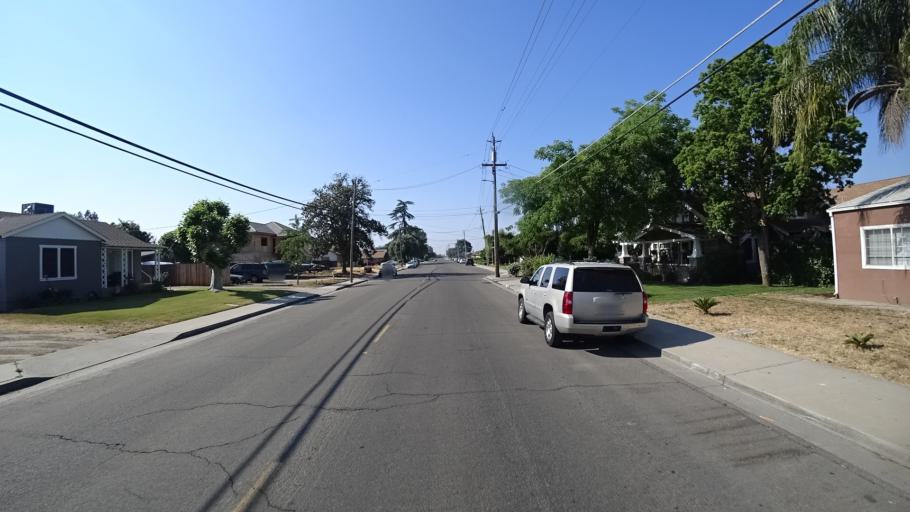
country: US
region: California
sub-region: Fresno County
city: Kingsburg
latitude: 36.5093
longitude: -119.5569
